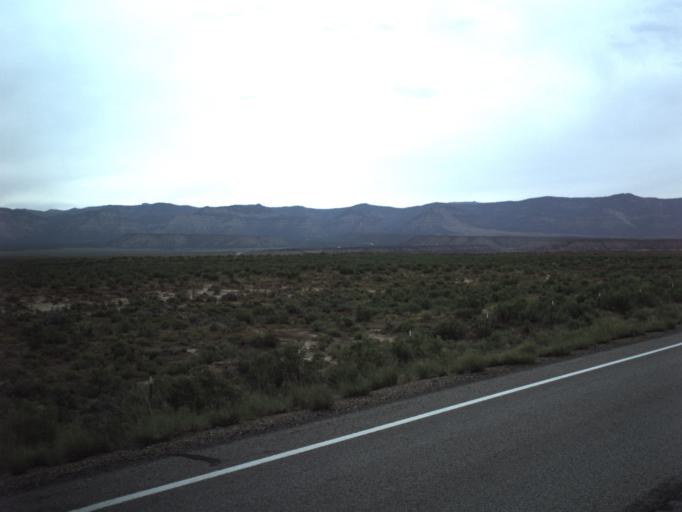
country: US
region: Utah
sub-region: Carbon County
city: East Carbon City
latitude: 39.5322
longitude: -110.5426
